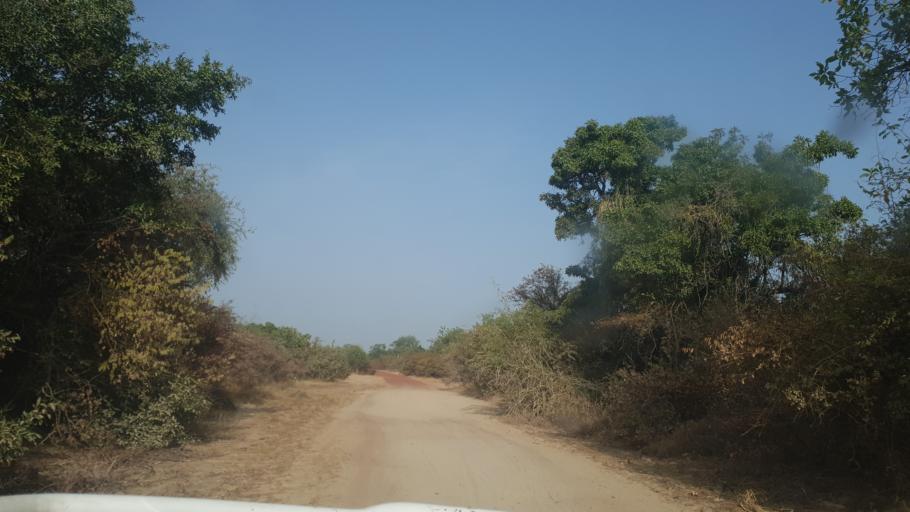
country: ML
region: Segou
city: Baroueli
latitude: 13.3726
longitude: -6.9138
